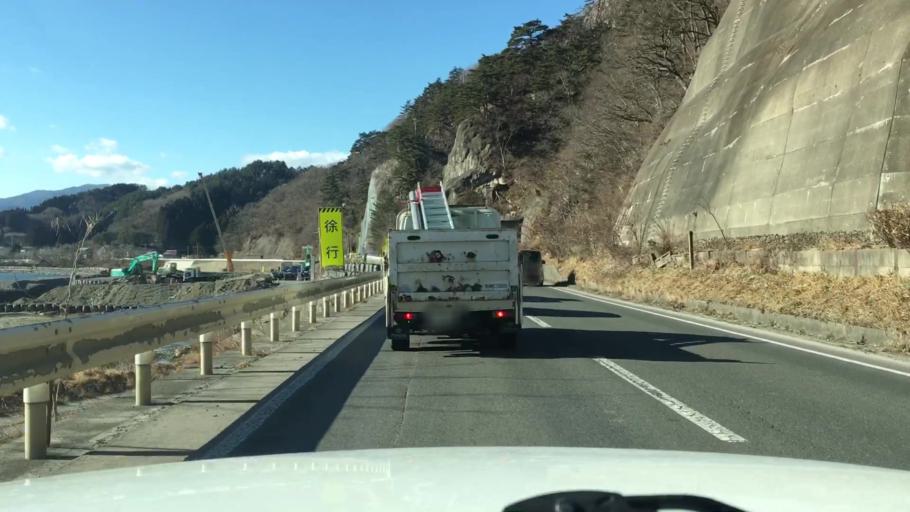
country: JP
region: Iwate
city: Miyako
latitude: 39.6317
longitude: 141.8699
